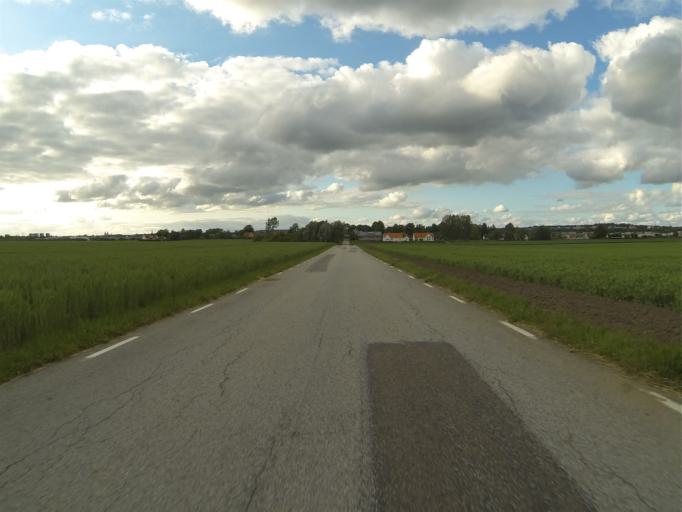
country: SE
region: Skane
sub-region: Lunds Kommun
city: Lund
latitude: 55.6818
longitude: 13.2256
